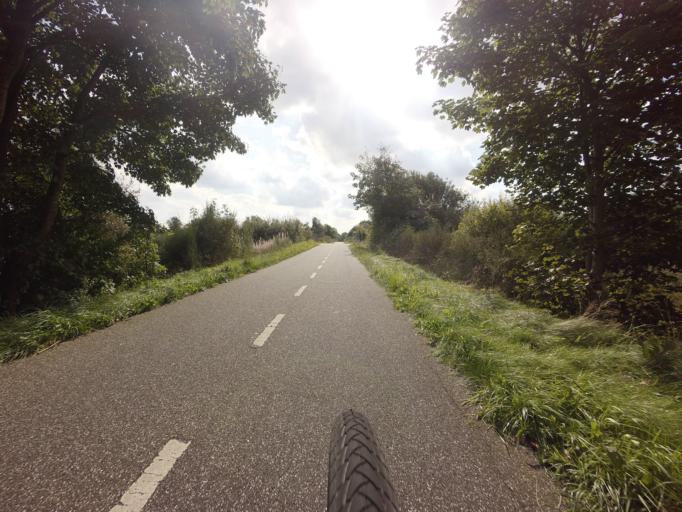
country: DK
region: Central Jutland
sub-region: Herning Kommune
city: Sunds
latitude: 56.1809
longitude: 9.0059
